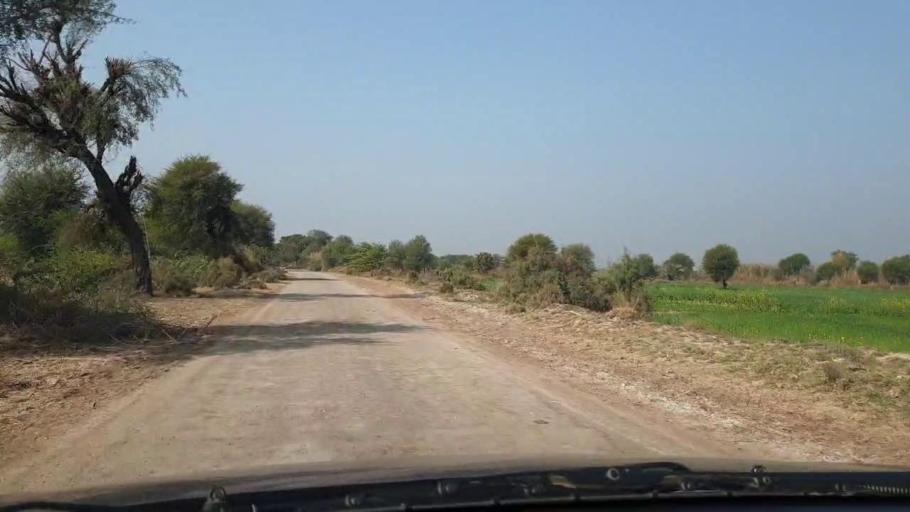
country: PK
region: Sindh
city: Jhol
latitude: 25.9611
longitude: 68.9445
